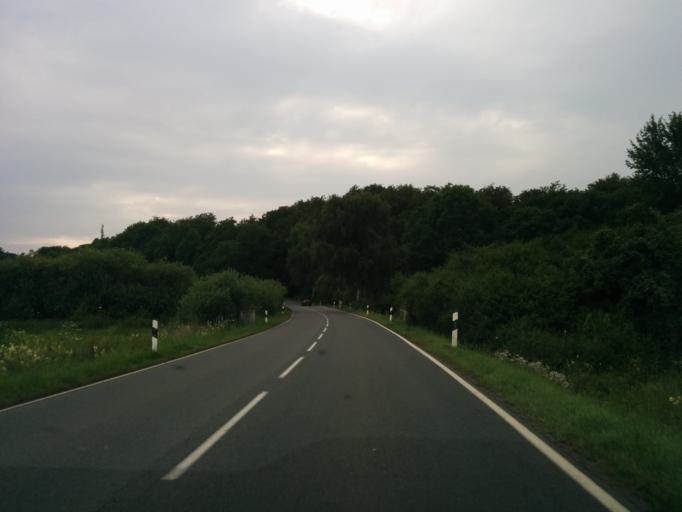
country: DE
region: Lower Saxony
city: Waake
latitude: 51.5944
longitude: 10.0501
